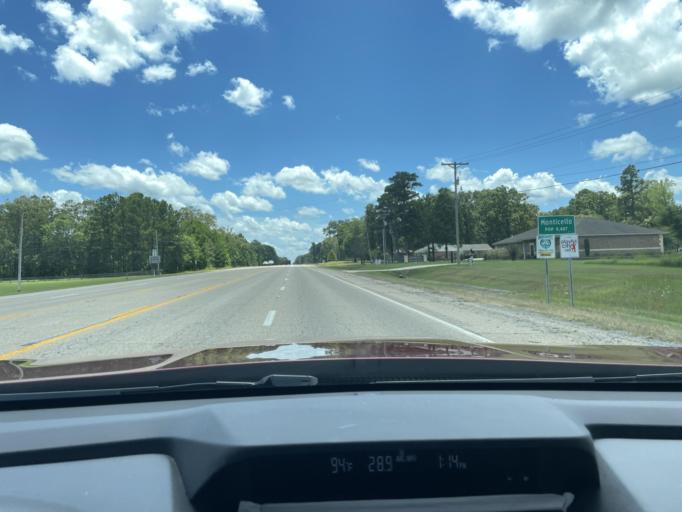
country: US
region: Arkansas
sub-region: Drew County
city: Monticello
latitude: 33.6680
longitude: -91.8040
